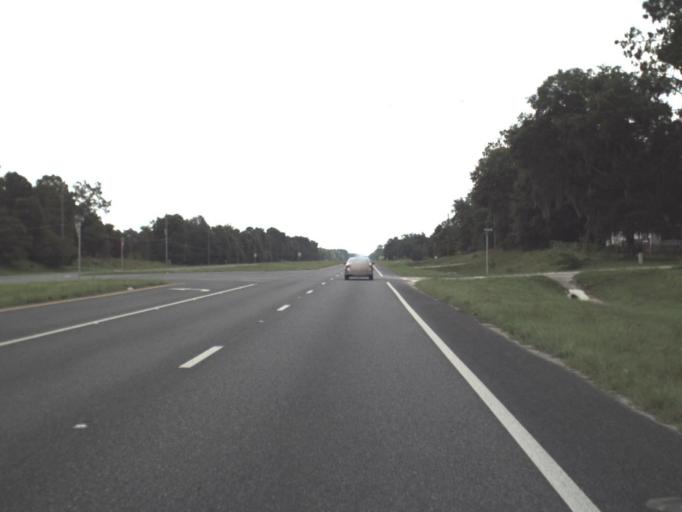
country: US
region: Florida
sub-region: Levy County
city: Williston Highlands
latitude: 29.4093
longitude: -82.5354
